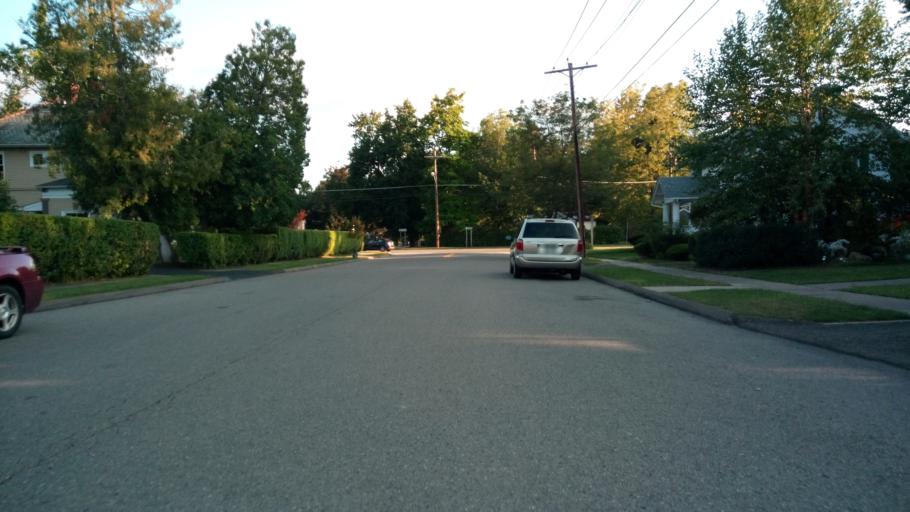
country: US
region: New York
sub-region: Chemung County
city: West Elmira
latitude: 42.0787
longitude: -76.8439
